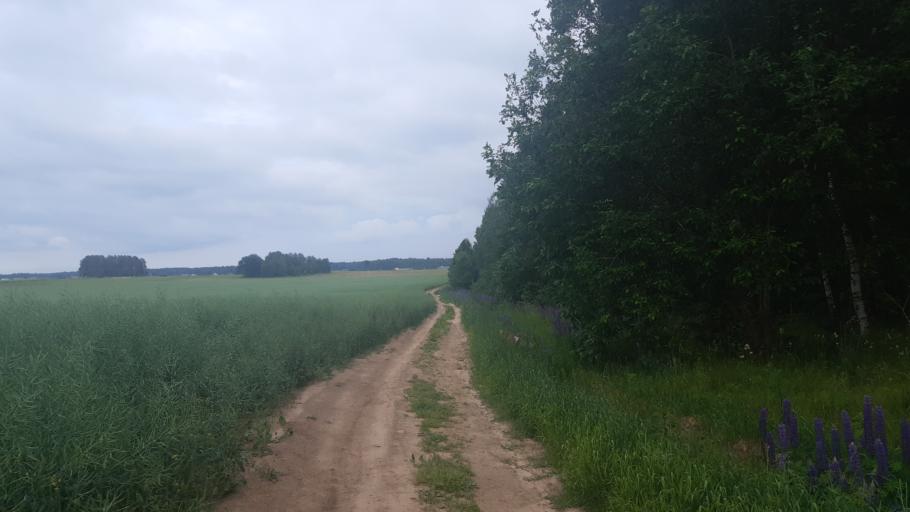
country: BY
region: Minsk
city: Horad Zhodzina
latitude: 54.1363
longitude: 28.2817
